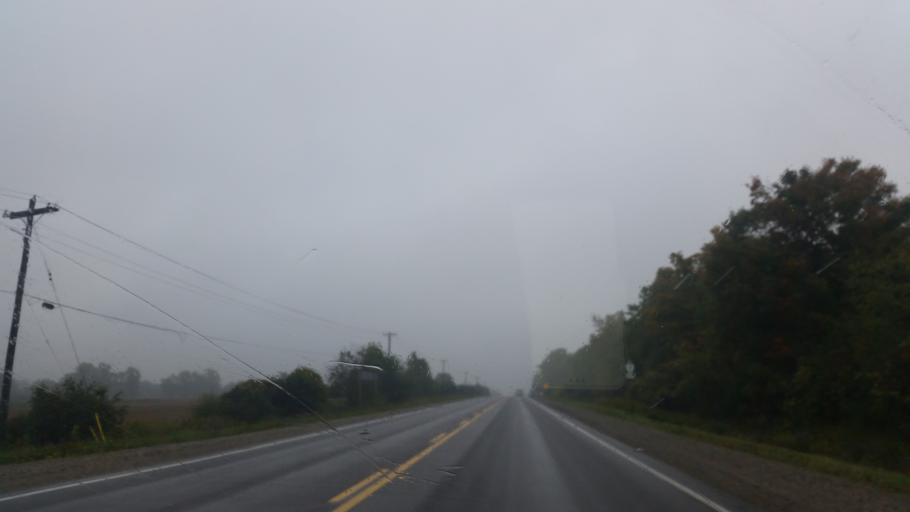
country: CA
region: Ontario
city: Stratford
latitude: 43.2767
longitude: -81.0625
